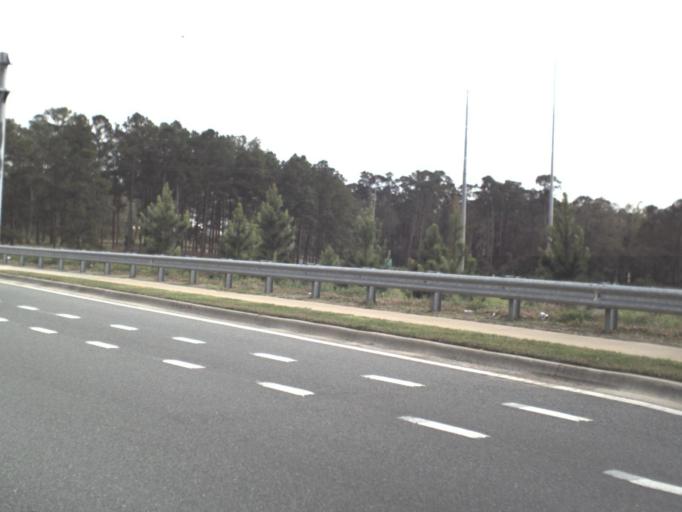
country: US
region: Florida
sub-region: Leon County
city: Tallahassee
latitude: 30.4832
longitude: -84.3104
